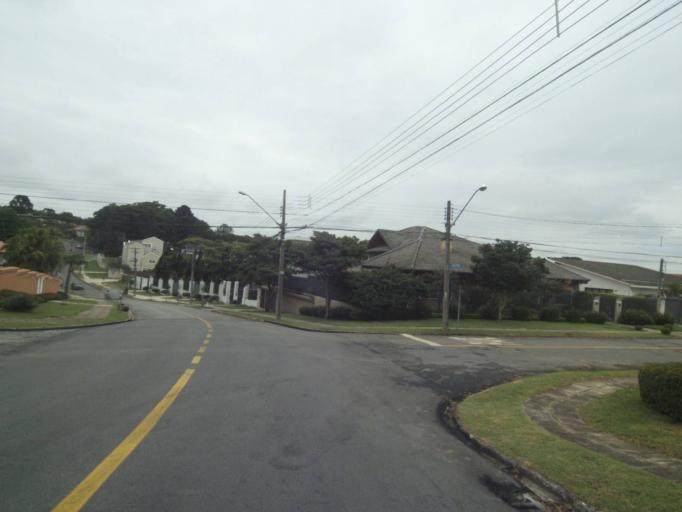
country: BR
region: Parana
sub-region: Curitiba
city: Curitiba
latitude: -25.4086
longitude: -49.2840
